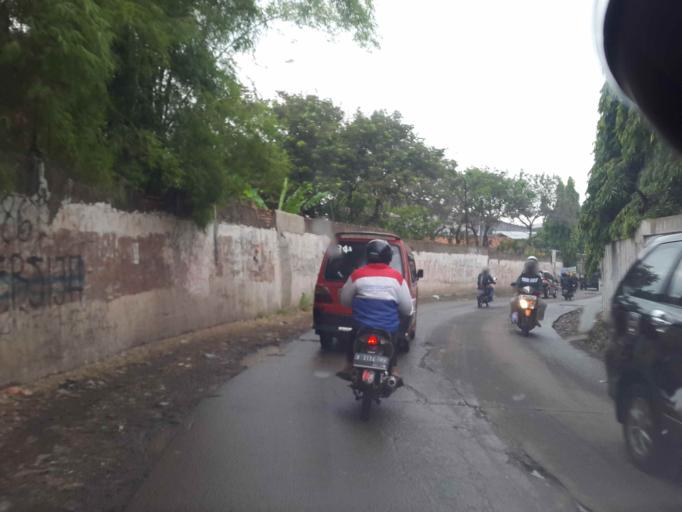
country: ID
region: West Java
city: Bekasi
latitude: -6.2563
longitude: 107.0414
